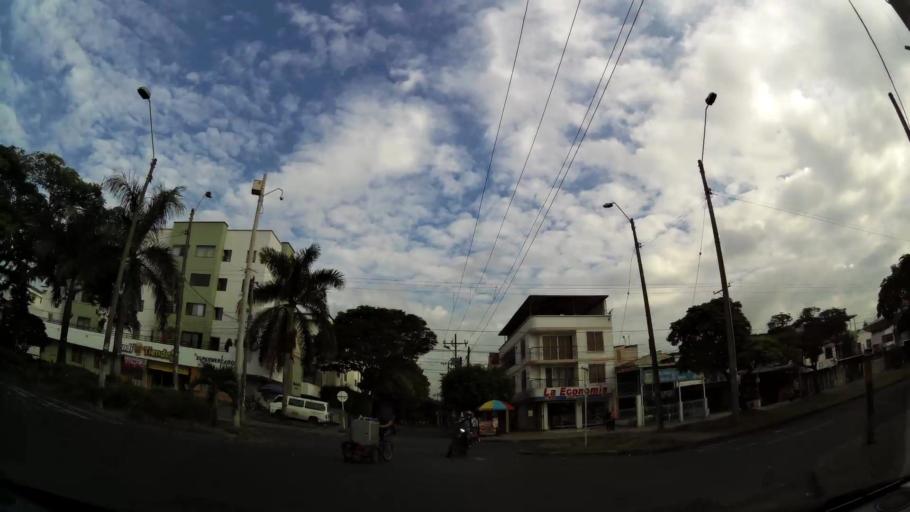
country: CO
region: Valle del Cauca
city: Cali
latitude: 3.4699
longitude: -76.4961
